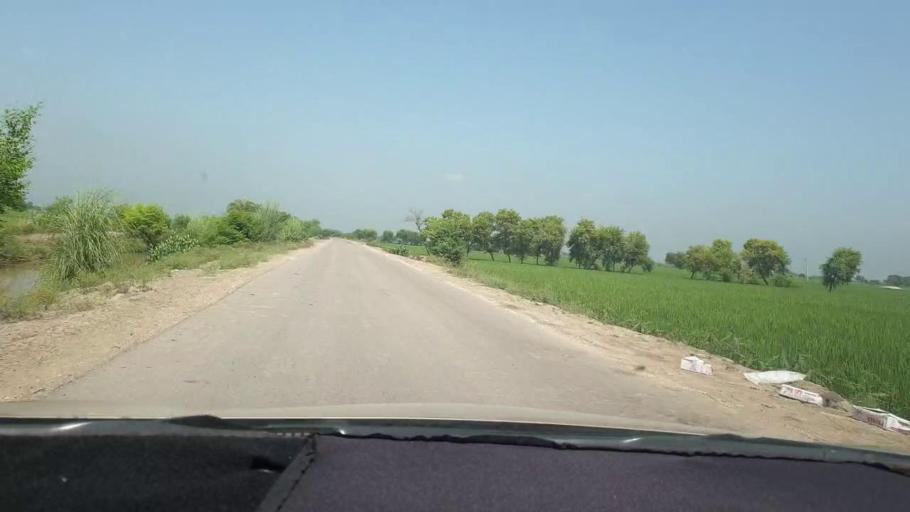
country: PK
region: Sindh
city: Miro Khan
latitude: 27.7600
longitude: 68.0788
